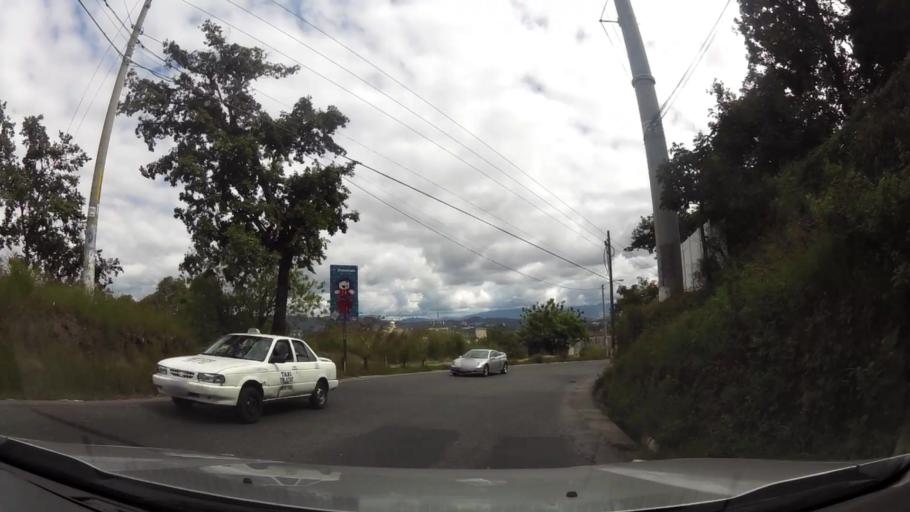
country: GT
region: Guatemala
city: Guatemala City
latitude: 14.6745
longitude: -90.5501
